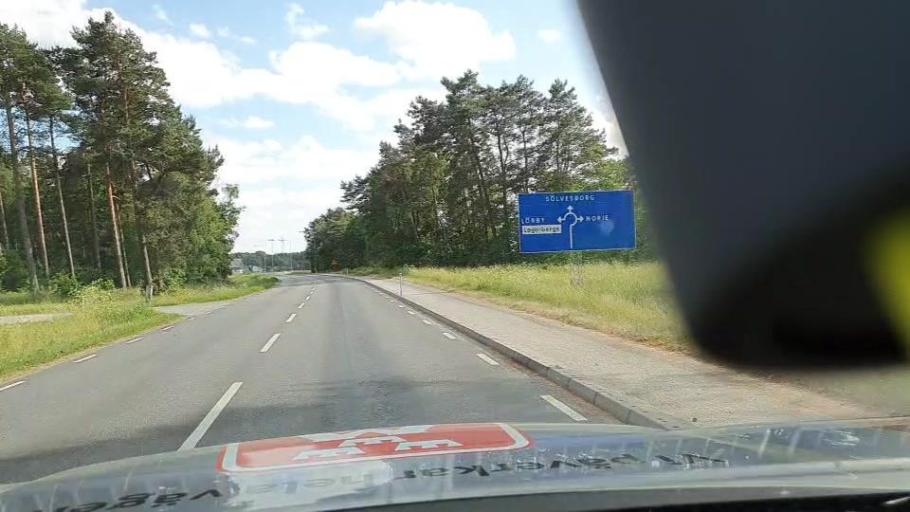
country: SE
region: Blekinge
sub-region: Karlshamns Kommun
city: Morrum
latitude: 56.1145
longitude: 14.6755
